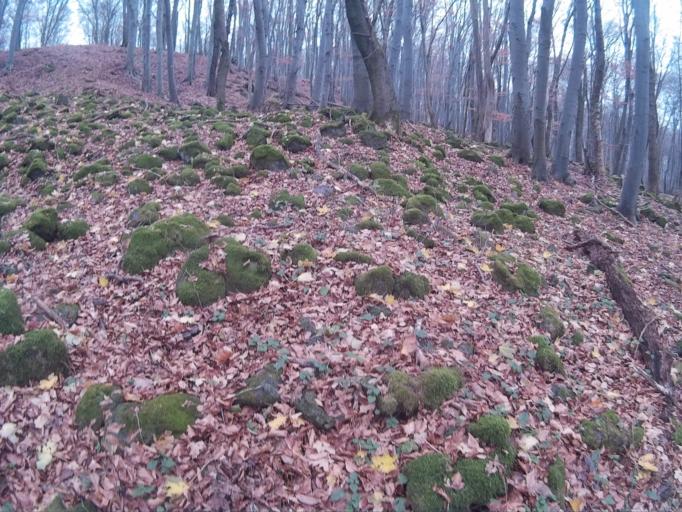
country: HU
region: Veszprem
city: Tapolca
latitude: 46.9771
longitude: 17.5079
